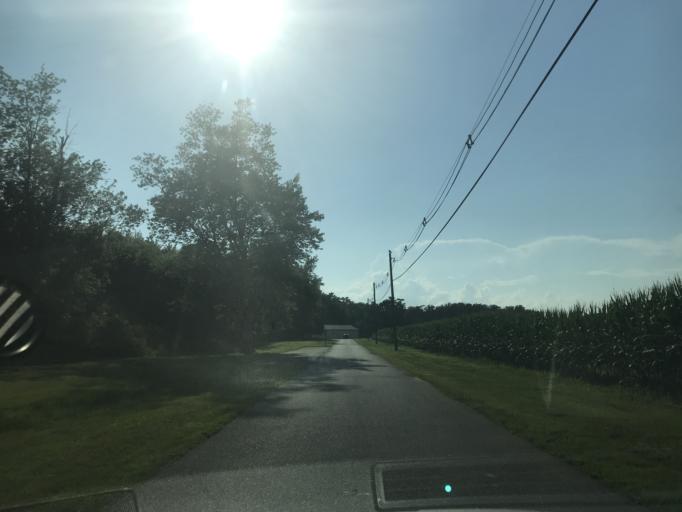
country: US
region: Maryland
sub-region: Harford County
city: Aberdeen Proving Ground
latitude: 39.5061
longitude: -76.1225
